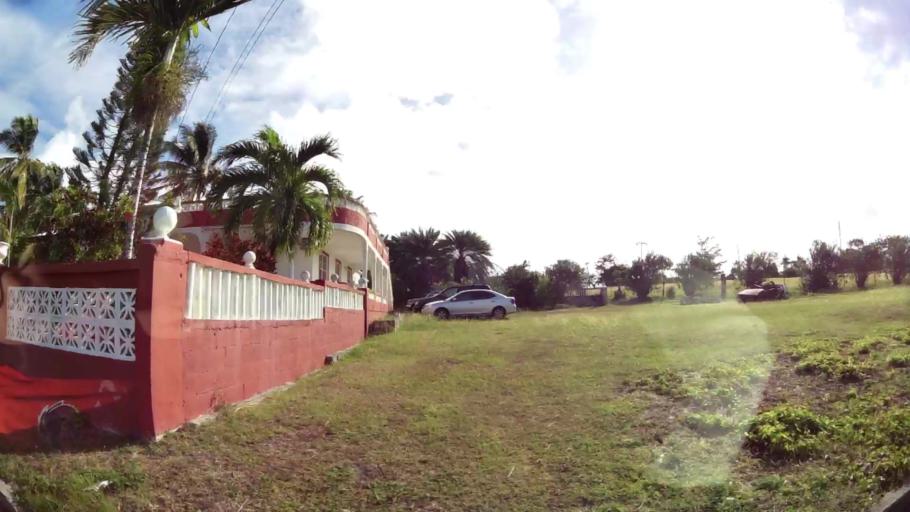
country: AG
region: Saint Peter
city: Parham
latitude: 17.0928
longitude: -61.7269
